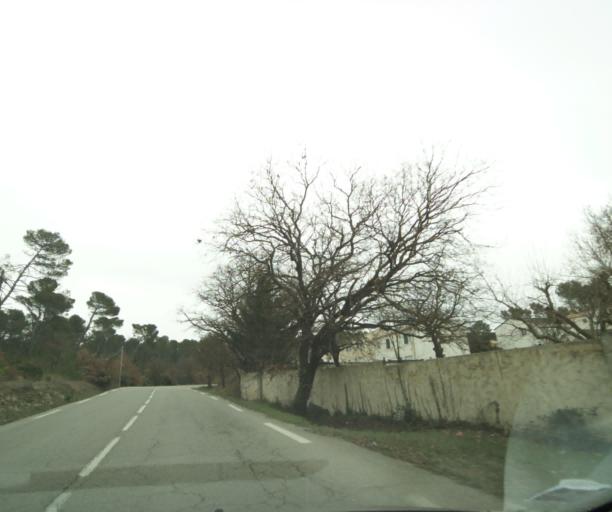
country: FR
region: Provence-Alpes-Cote d'Azur
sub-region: Departement des Bouches-du-Rhone
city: Greasque
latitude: 43.4403
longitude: 5.5553
